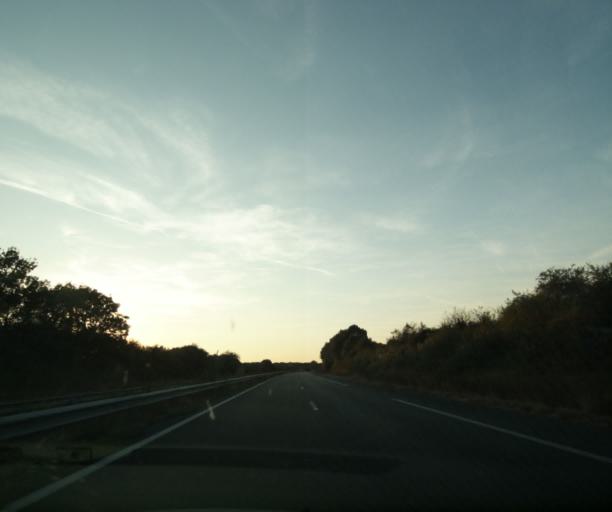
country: FR
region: Aquitaine
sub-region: Departement du Lot-et-Garonne
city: Fourques-sur-Garonne
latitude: 44.3804
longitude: 0.2119
